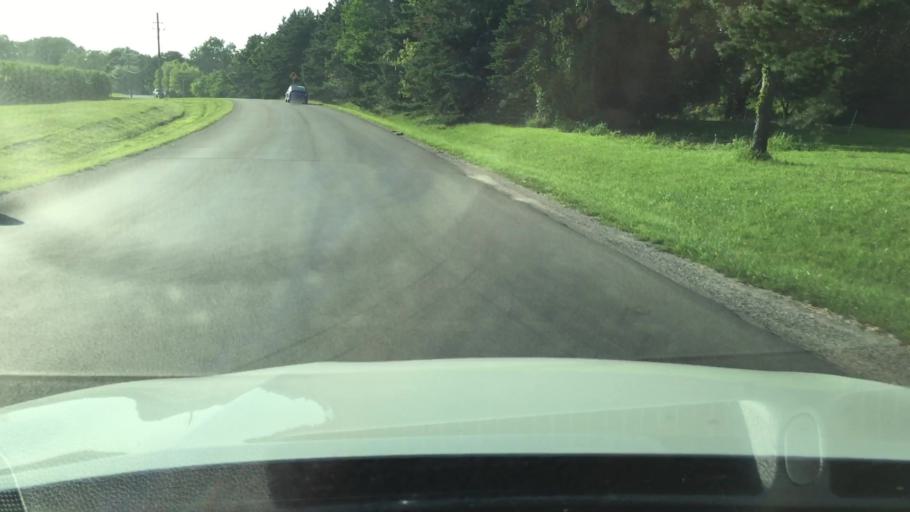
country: US
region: Iowa
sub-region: Linn County
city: Ely
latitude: 41.8151
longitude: -91.6165
